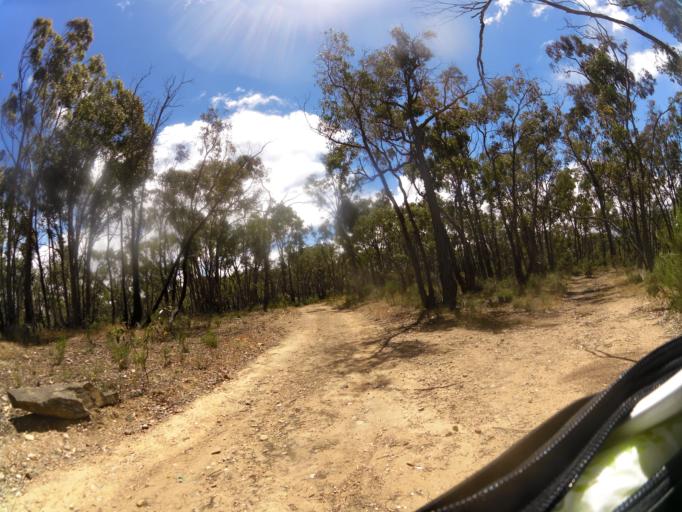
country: AU
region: Victoria
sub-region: Mount Alexander
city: Castlemaine
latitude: -37.0700
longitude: 144.2646
